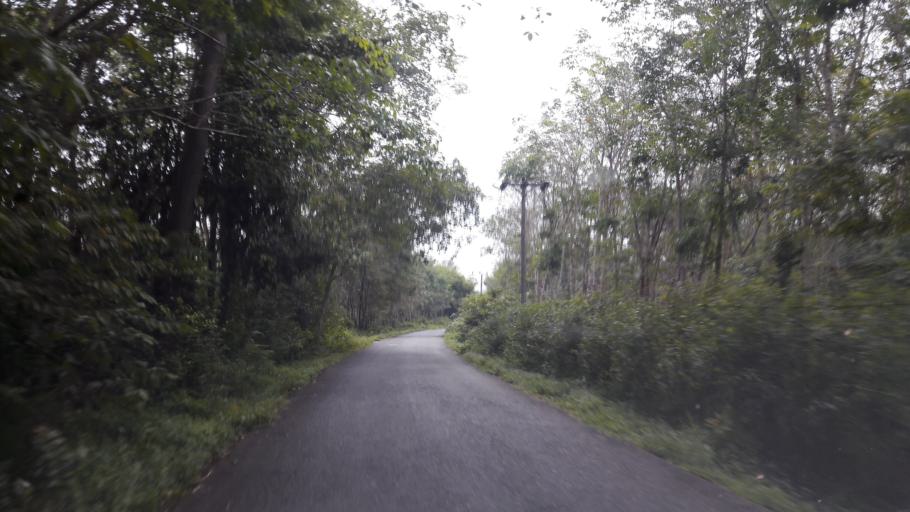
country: ID
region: South Sumatra
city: Gunungmenang
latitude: -3.1199
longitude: 104.0953
